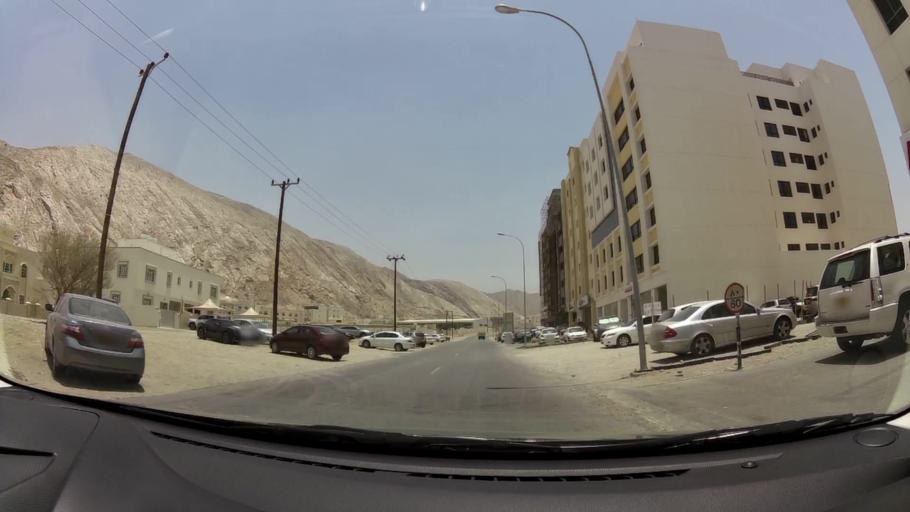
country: OM
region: Muhafazat Masqat
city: Bawshar
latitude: 23.5631
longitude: 58.4199
